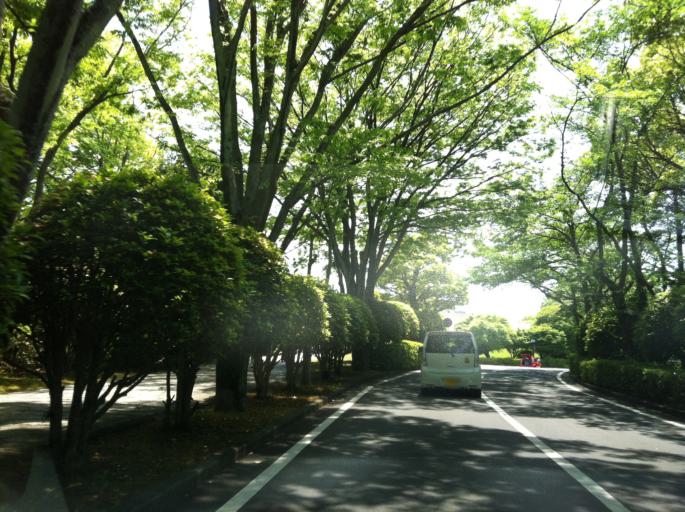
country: JP
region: Shizuoka
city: Shizuoka-shi
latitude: 34.9930
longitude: 138.4447
